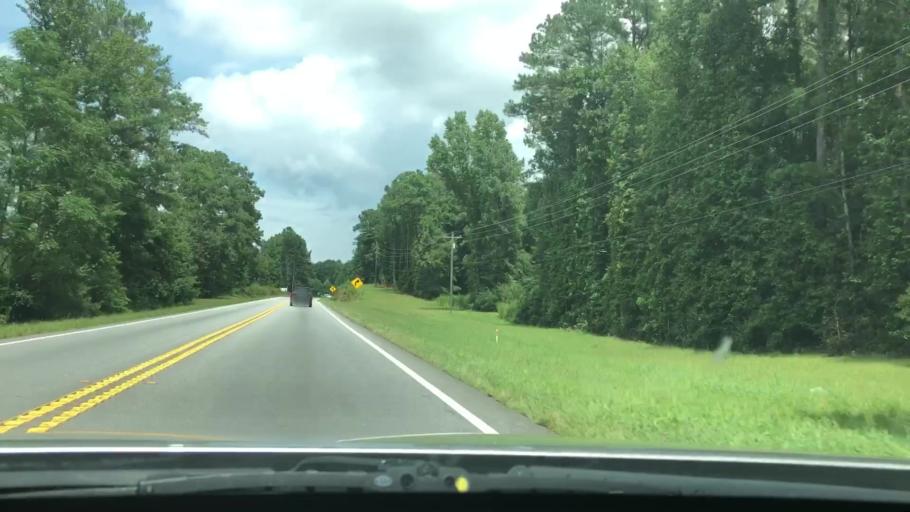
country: US
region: Georgia
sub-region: Lamar County
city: Barnesville
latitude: 33.1474
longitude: -84.1448
